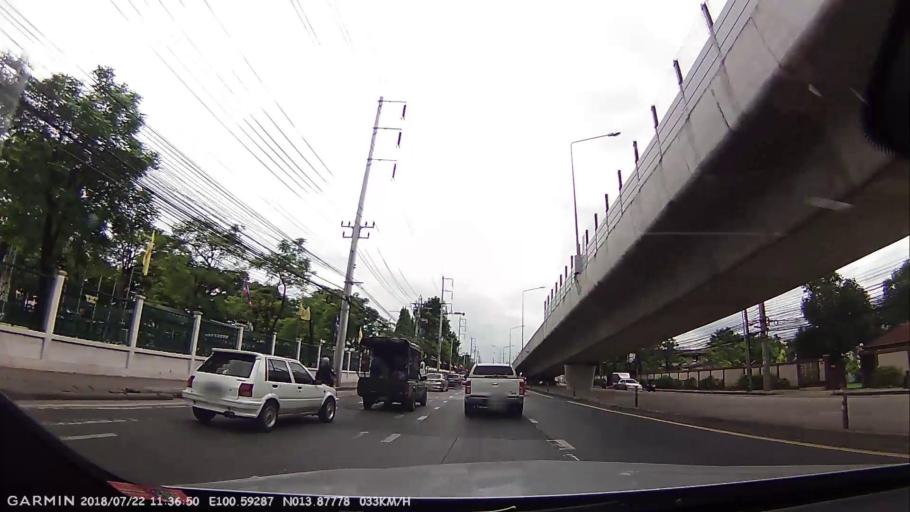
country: TH
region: Bangkok
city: Lak Si
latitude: 13.8778
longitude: 100.5928
